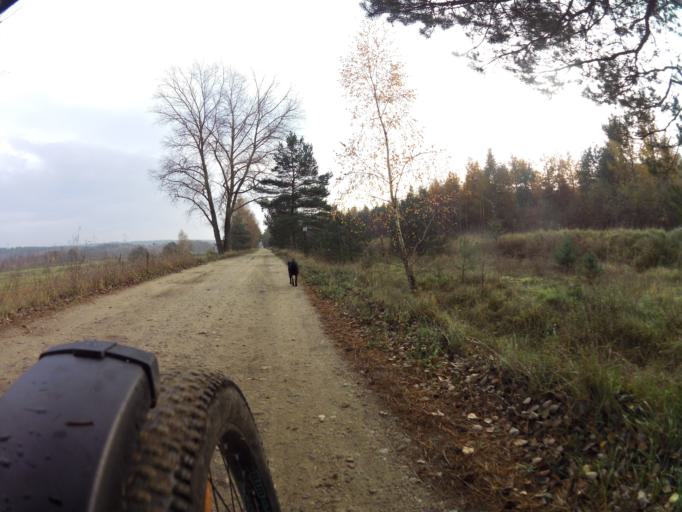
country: PL
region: Pomeranian Voivodeship
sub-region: Powiat wejherowski
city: Gniewino
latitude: 54.7037
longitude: 18.1060
